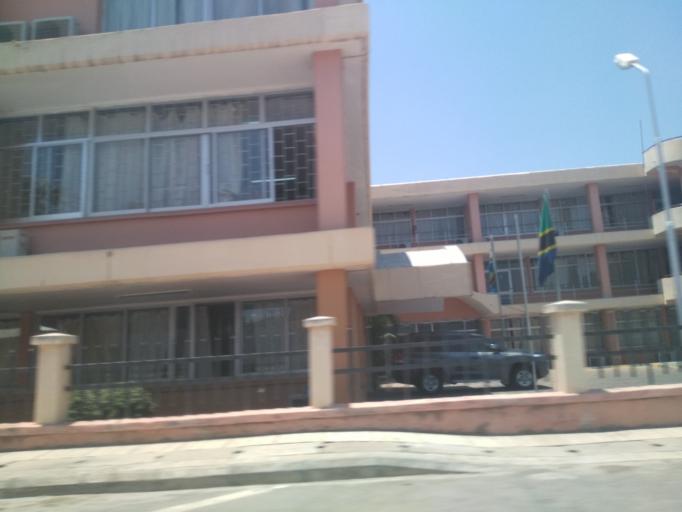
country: TZ
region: Dodoma
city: Dodoma
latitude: -6.1813
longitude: 35.7462
